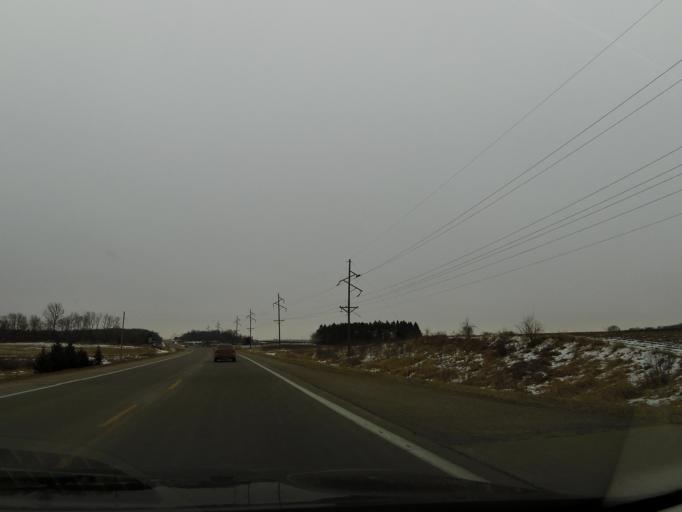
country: US
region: Minnesota
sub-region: Scott County
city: Jordan
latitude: 44.6462
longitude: -93.6261
